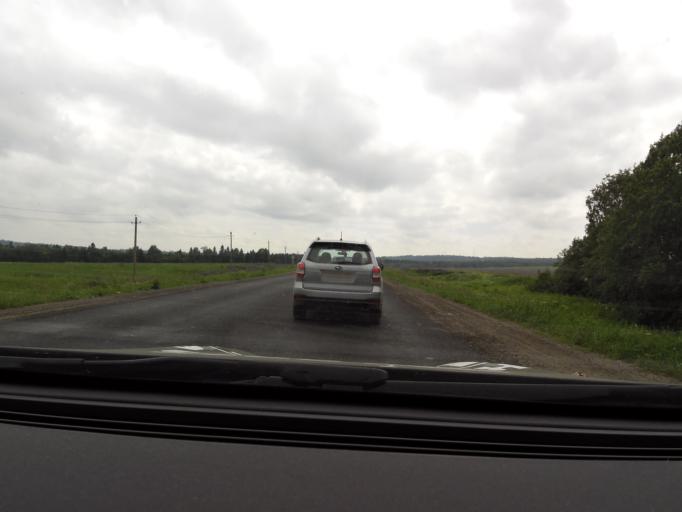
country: RU
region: Perm
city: Zvezdnyy
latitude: 57.7786
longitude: 56.3462
